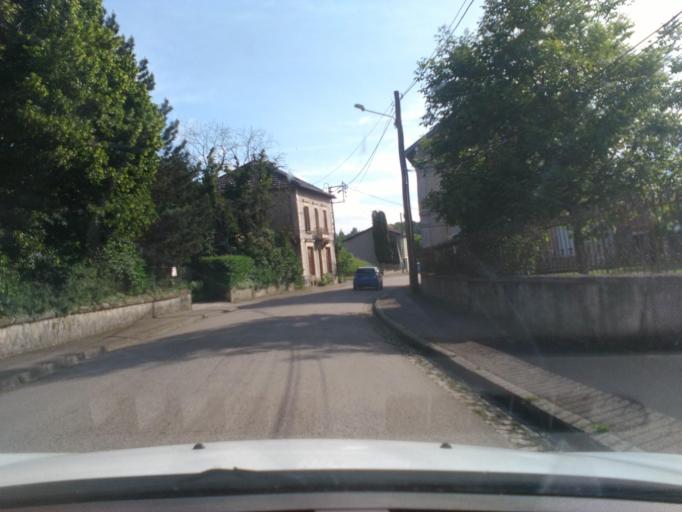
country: FR
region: Lorraine
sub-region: Departement de Meurthe-et-Moselle
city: Baccarat
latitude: 48.4895
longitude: 6.6957
